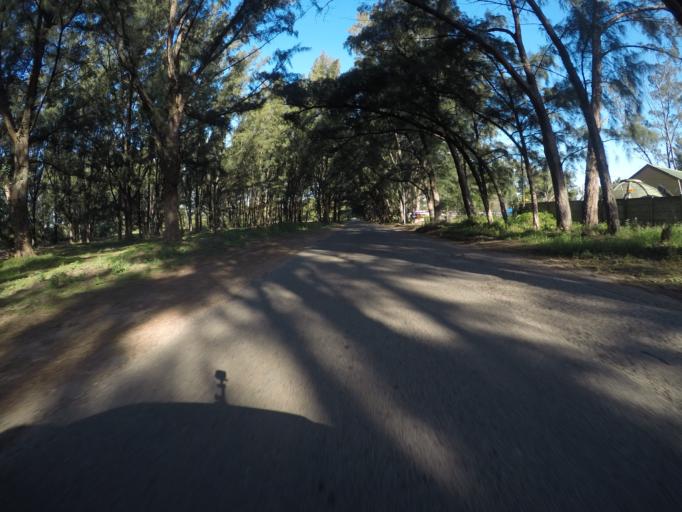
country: ZA
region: KwaZulu-Natal
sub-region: uThungulu District Municipality
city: Richards Bay
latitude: -28.7889
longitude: 32.0838
